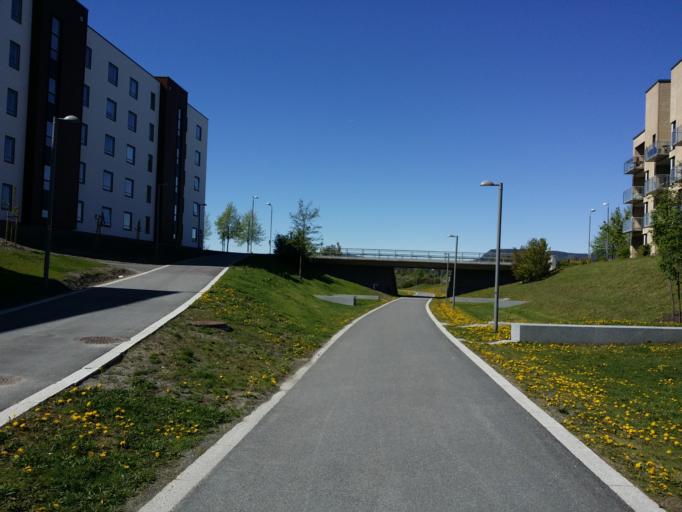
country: NO
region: Akershus
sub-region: Baerum
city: Lysaker
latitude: 59.8968
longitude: 10.6234
